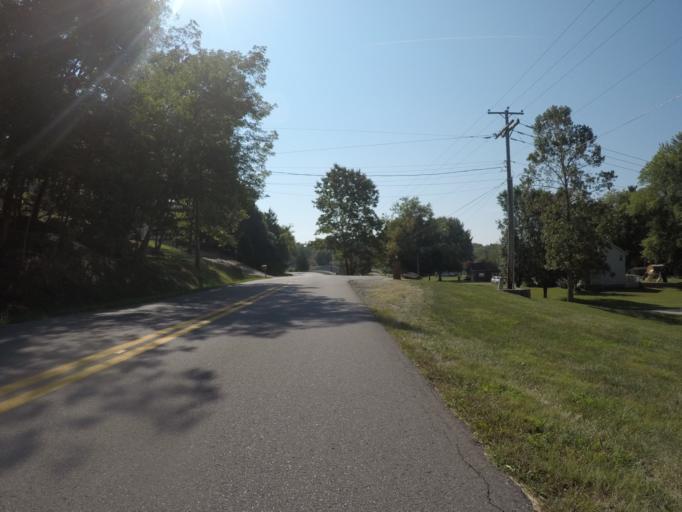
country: US
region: West Virginia
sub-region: Cabell County
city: Barboursville
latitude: 38.3795
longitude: -82.2822
